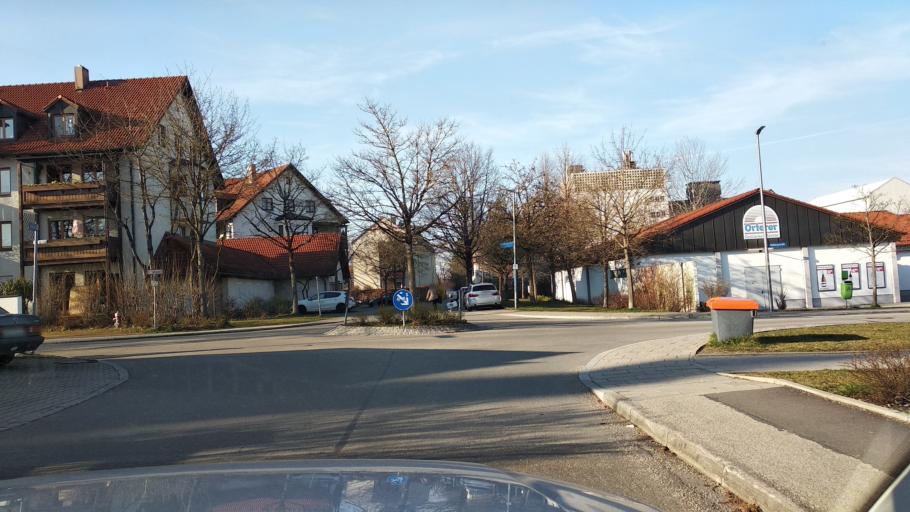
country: DE
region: Bavaria
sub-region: Upper Bavaria
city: Markt Schwaben
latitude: 48.1860
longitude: 11.8675
